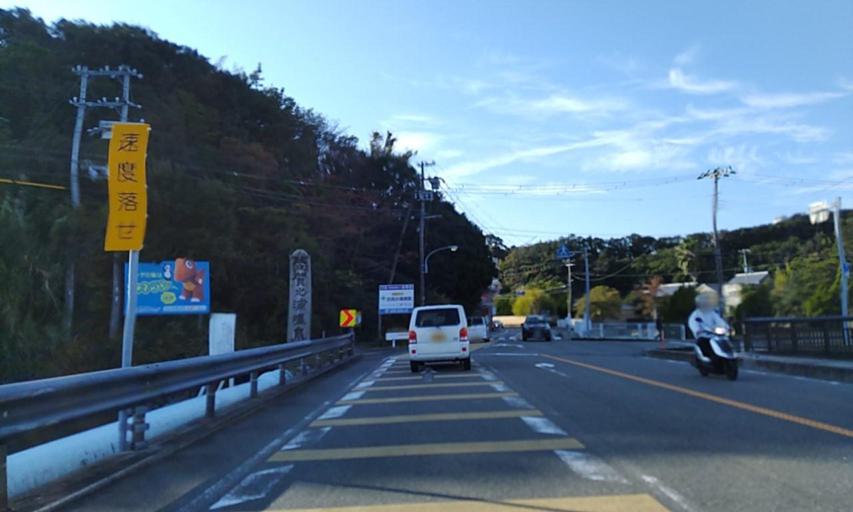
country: JP
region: Wakayama
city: Tanabe
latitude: 33.6799
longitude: 135.3592
